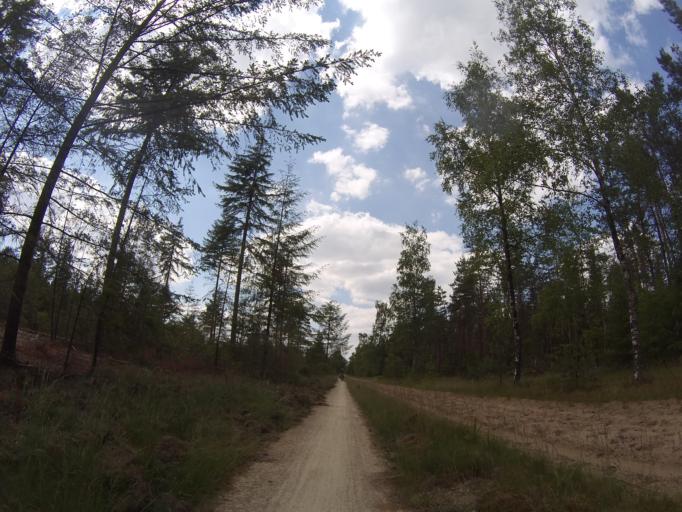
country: NL
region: Gelderland
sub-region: Gemeente Ede
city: Harskamp
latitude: 52.1864
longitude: 5.7526
